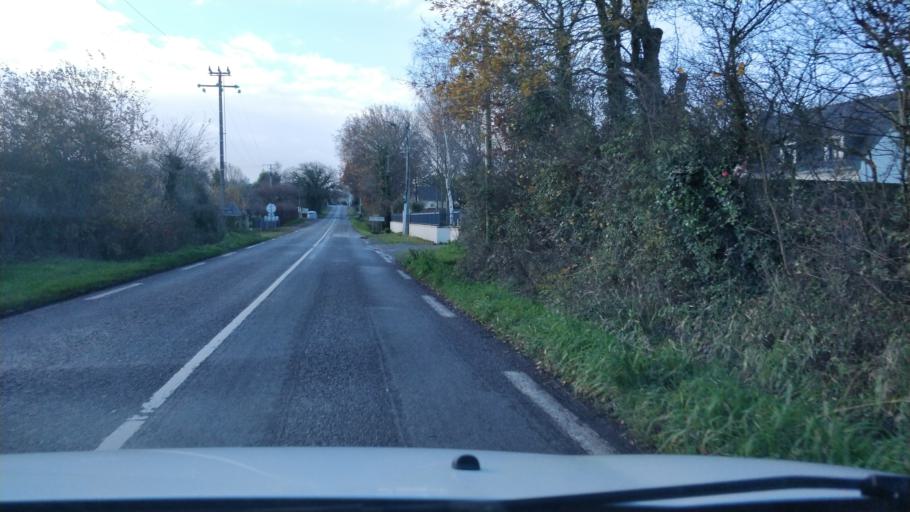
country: FR
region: Pays de la Loire
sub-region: Departement de la Loire-Atlantique
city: Asserac
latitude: 47.4191
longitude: -2.3991
